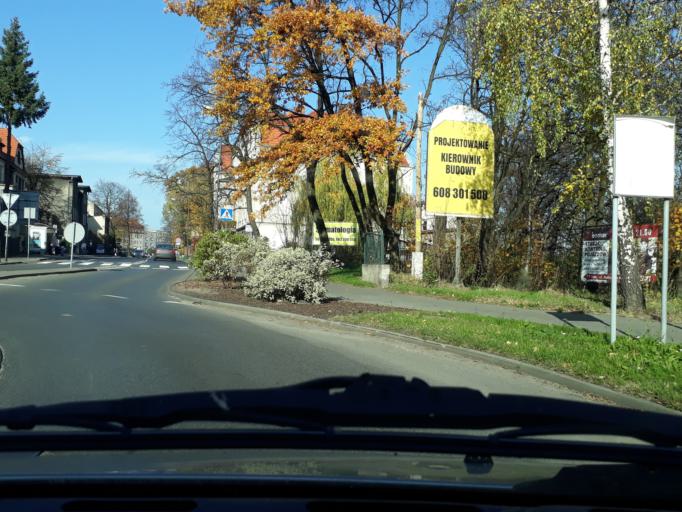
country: PL
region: Silesian Voivodeship
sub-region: Powiat tarnogorski
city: Tarnowskie Gory
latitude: 50.4405
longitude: 18.8614
